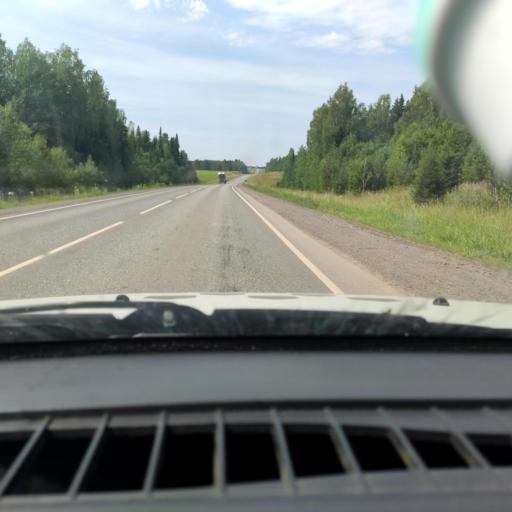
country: RU
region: Perm
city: Siva
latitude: 58.5130
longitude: 54.0231
